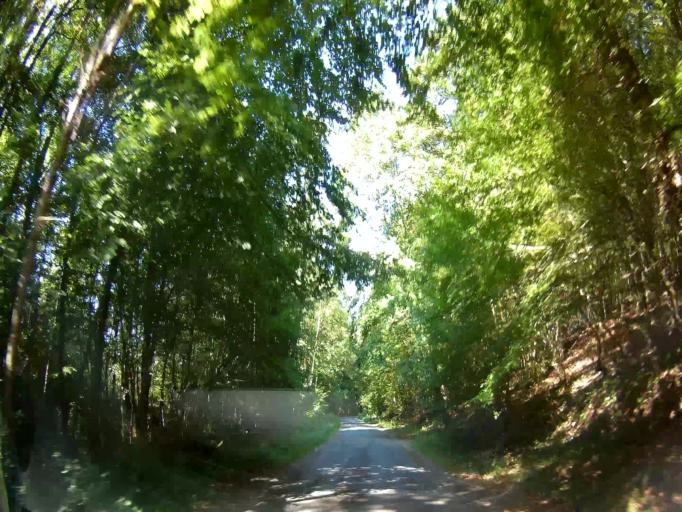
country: BE
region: Wallonia
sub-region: Province de Namur
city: Houyet
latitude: 50.2274
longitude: 4.9813
